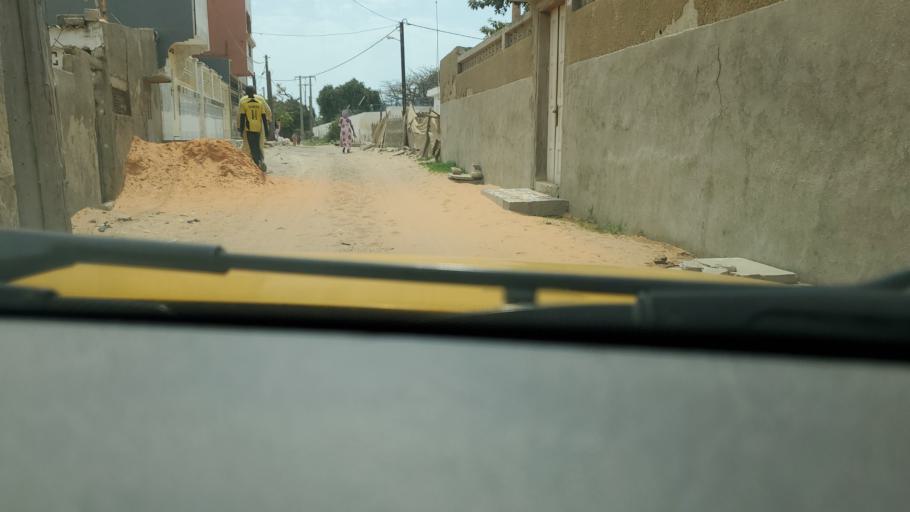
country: SN
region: Saint-Louis
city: Saint-Louis
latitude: 16.0258
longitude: -16.4749
